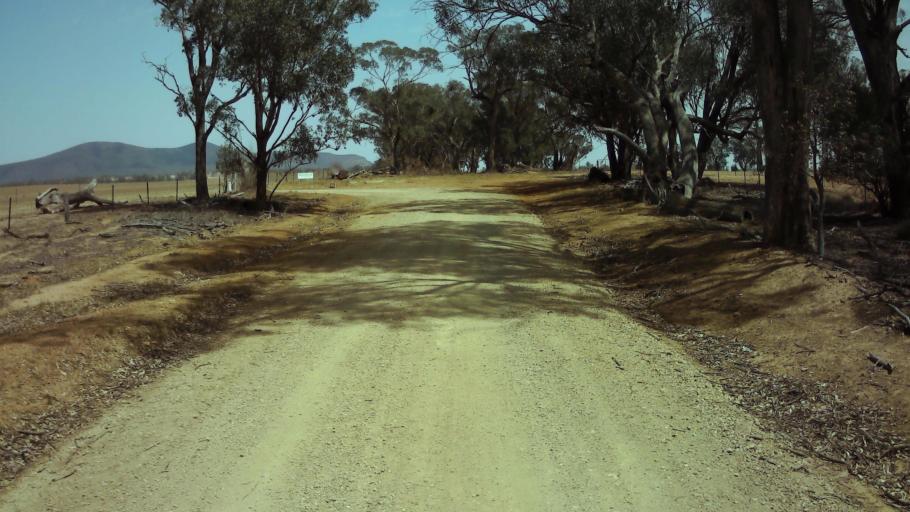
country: AU
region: New South Wales
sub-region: Weddin
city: Grenfell
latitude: -33.8828
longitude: 148.0682
